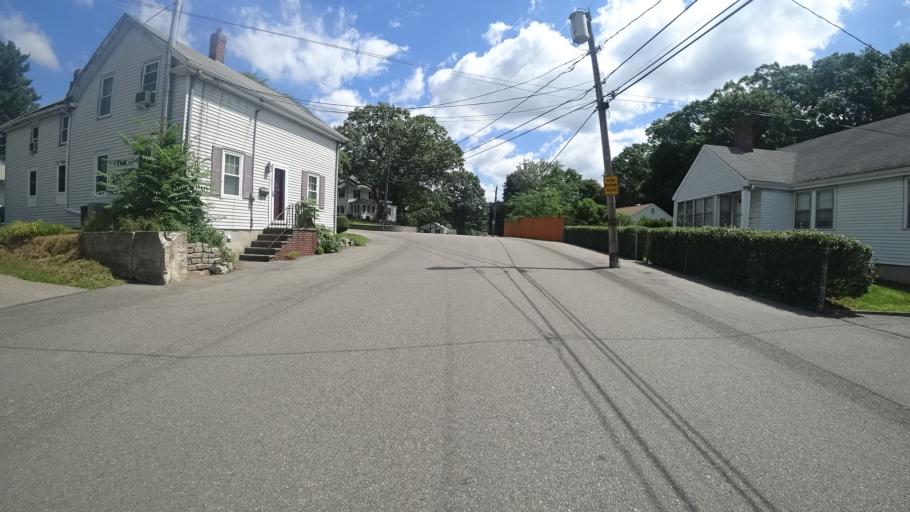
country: US
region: Massachusetts
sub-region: Norfolk County
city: Dedham
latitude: 42.2544
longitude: -71.1609
